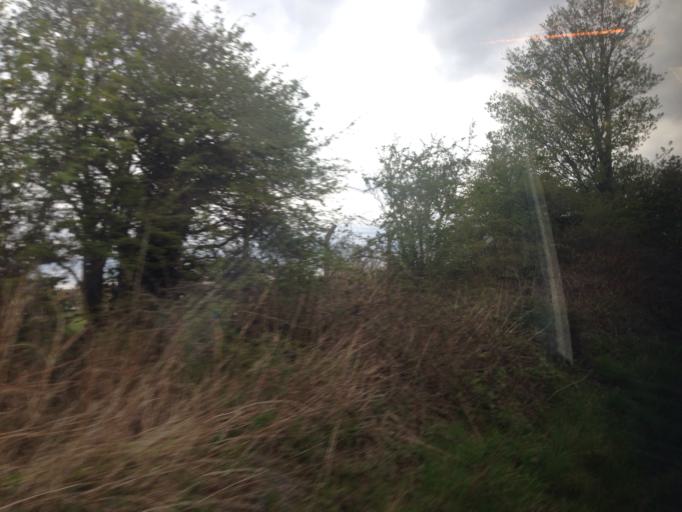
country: GB
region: England
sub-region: Greater London
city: Mitcham
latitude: 51.4005
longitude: -0.1587
